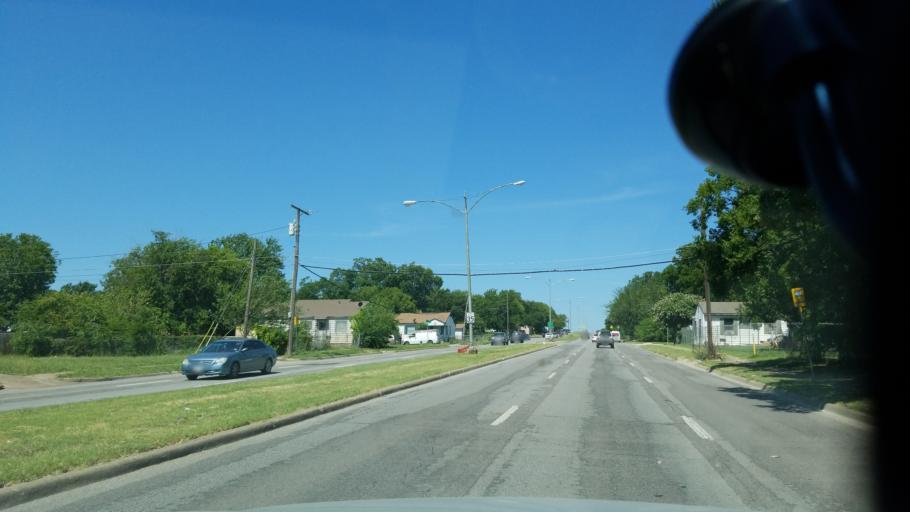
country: US
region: Texas
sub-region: Dallas County
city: Cockrell Hill
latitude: 32.7060
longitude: -96.8172
